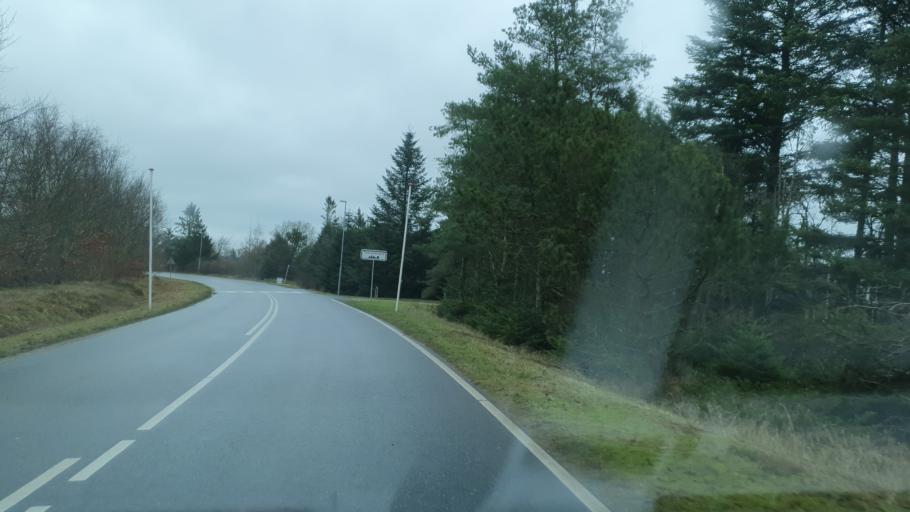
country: DK
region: North Denmark
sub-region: Jammerbugt Kommune
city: Fjerritslev
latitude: 57.1297
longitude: 9.1332
